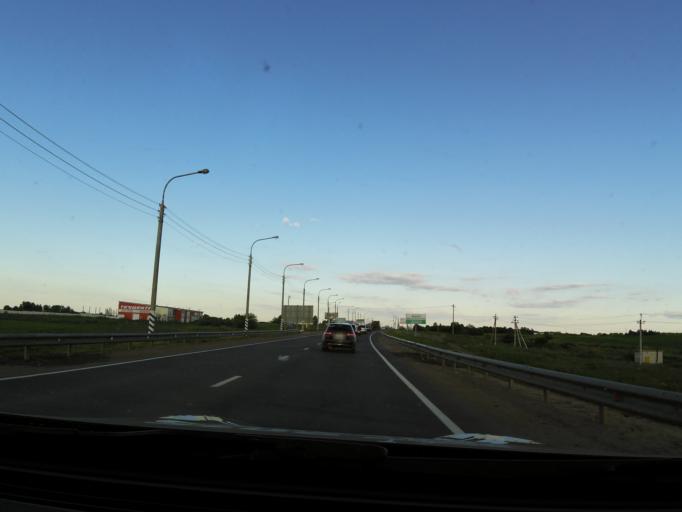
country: RU
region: Vologda
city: Vologda
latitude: 59.1746
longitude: 39.8983
